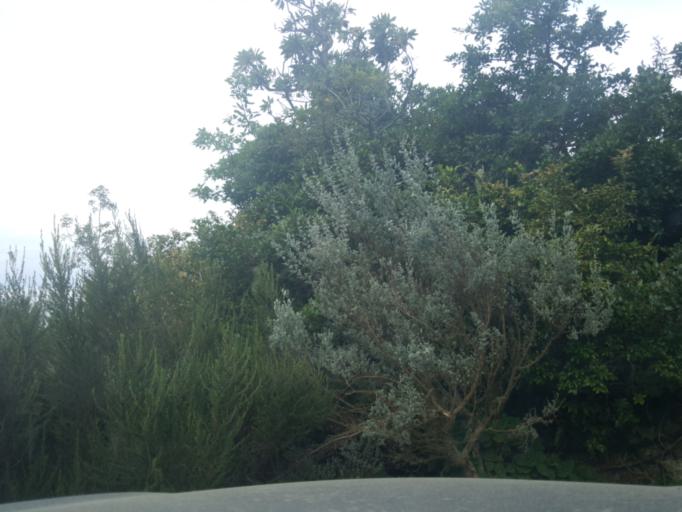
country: ZA
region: Limpopo
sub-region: Mopani District Municipality
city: Hoedspruit
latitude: -24.5386
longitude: 30.8711
